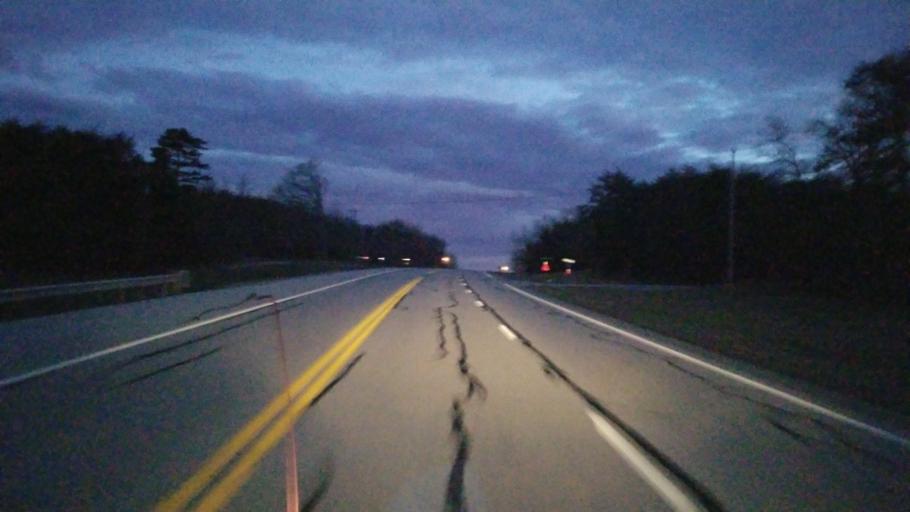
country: US
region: Tennessee
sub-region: Sequatchie County
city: Dunlap
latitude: 35.5085
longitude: -85.4742
